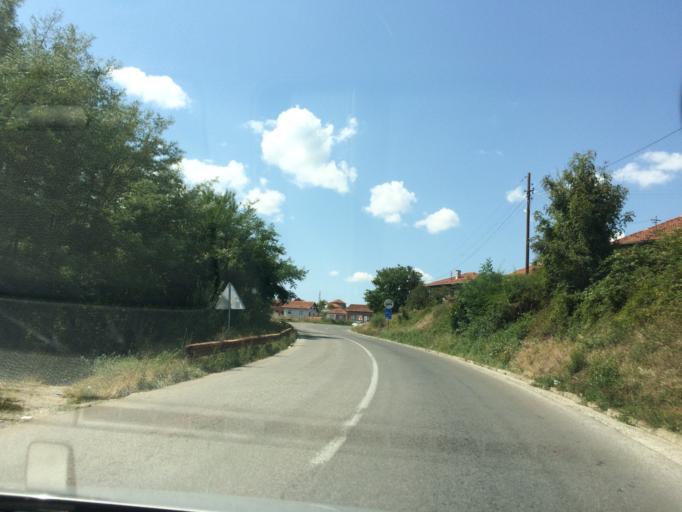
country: RS
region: Central Serbia
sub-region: Zlatiborski Okrug
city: Prijepolje
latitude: 43.3602
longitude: 19.6283
